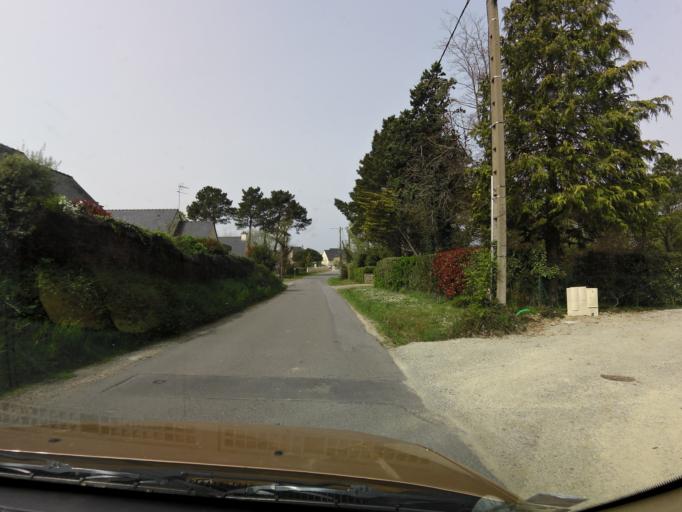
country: FR
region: Brittany
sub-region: Departement du Morbihan
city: Sene
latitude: 47.5755
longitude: -2.7099
